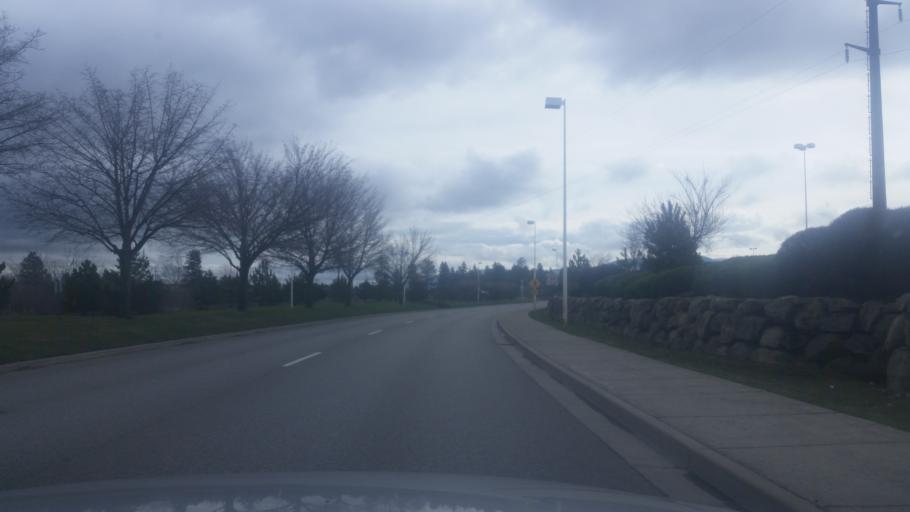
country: US
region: Washington
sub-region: Spokane County
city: Trentwood
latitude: 47.6762
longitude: -117.2087
